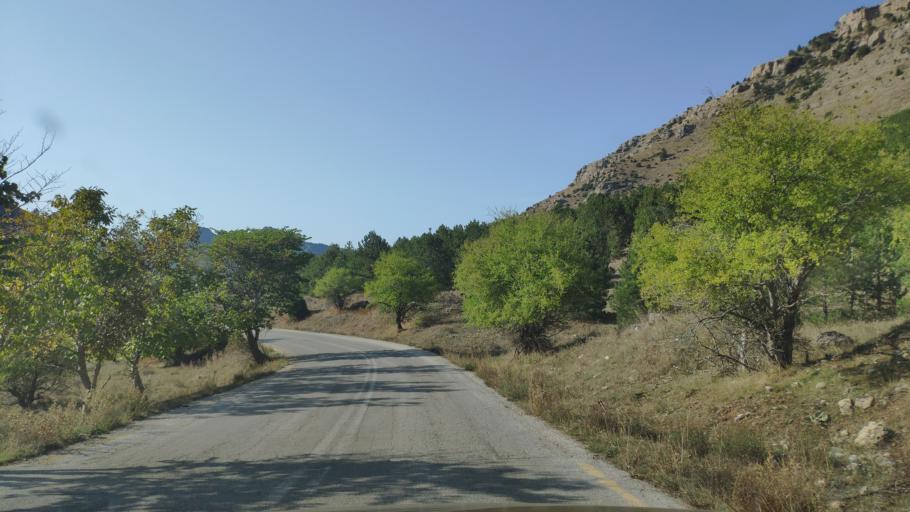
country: GR
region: West Greece
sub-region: Nomos Achaias
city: Aiyira
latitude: 38.0395
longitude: 22.3963
